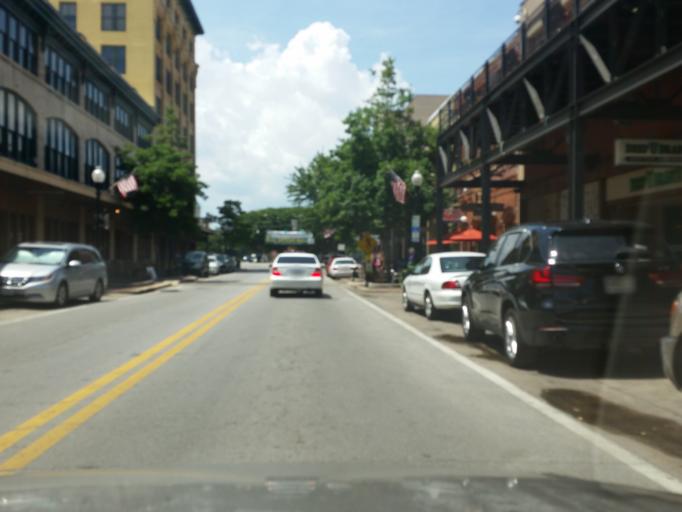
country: US
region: Florida
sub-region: Escambia County
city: Pensacola
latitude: 30.4119
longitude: -87.2152
